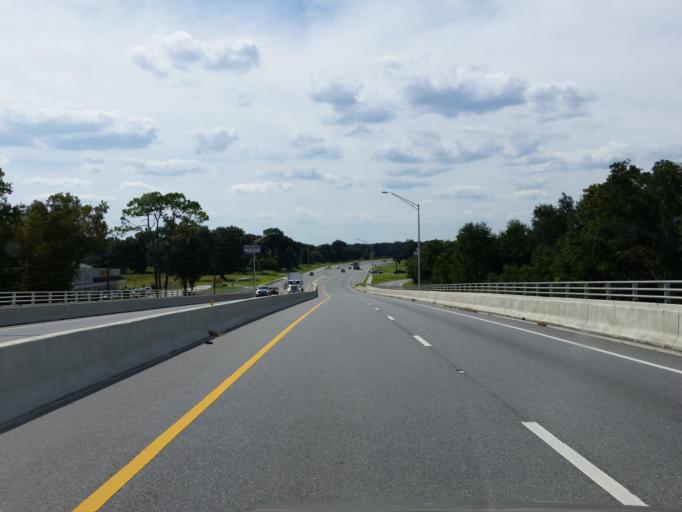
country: US
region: Florida
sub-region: Sumter County
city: Wildwood
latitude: 28.8473
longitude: -82.0508
